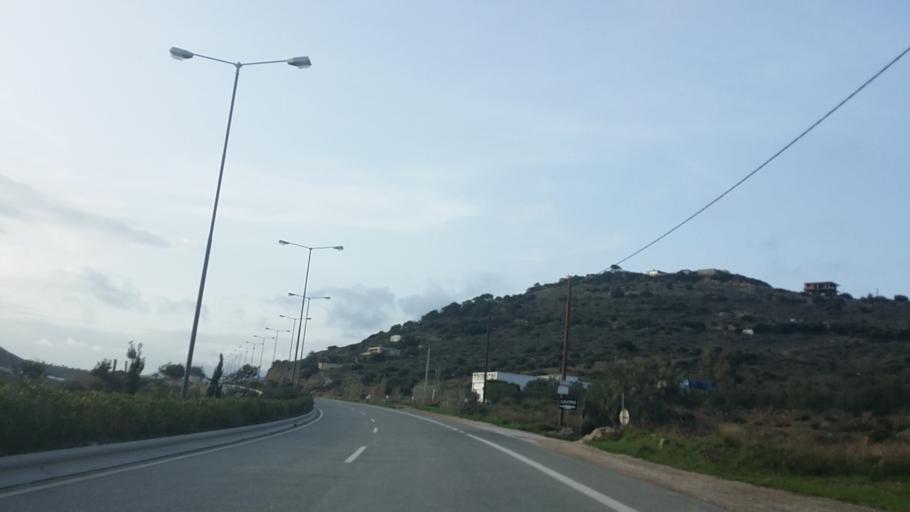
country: GR
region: Attica
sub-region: Nomarchia Anatolikis Attikis
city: Lavrio
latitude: 37.7932
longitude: 24.0557
